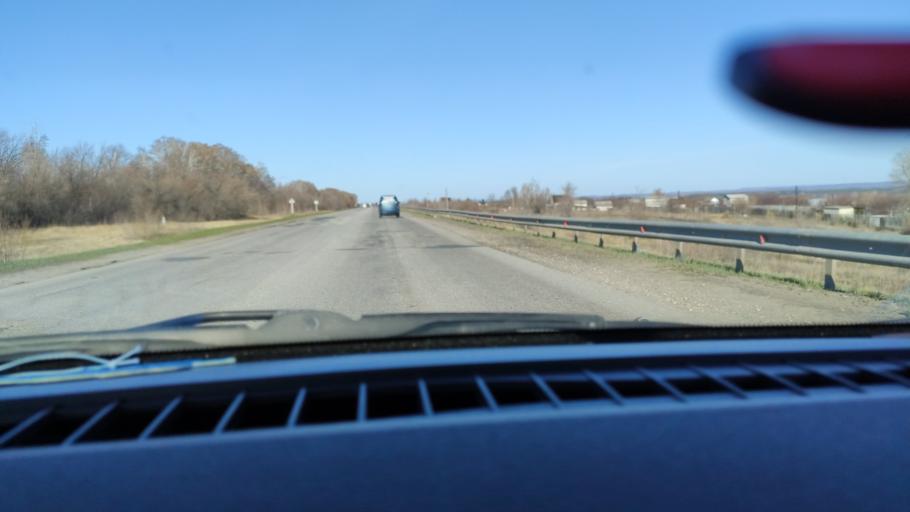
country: RU
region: Samara
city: Varlamovo
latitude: 53.1218
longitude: 48.3179
